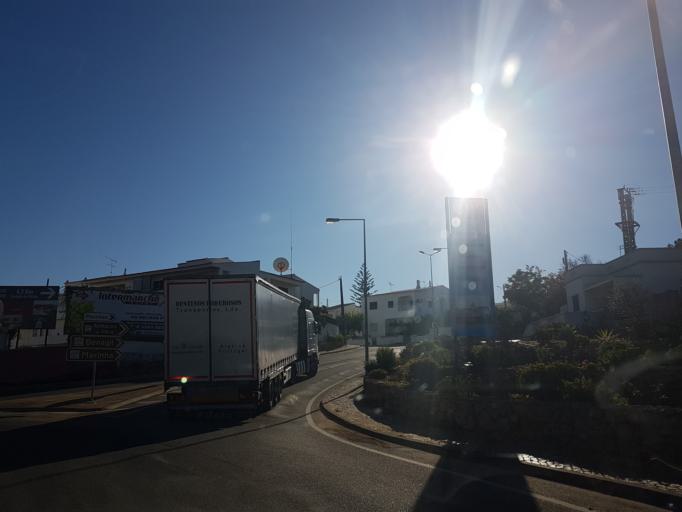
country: PT
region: Faro
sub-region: Silves
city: Armacao de Pera
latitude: 37.1267
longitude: -8.4021
